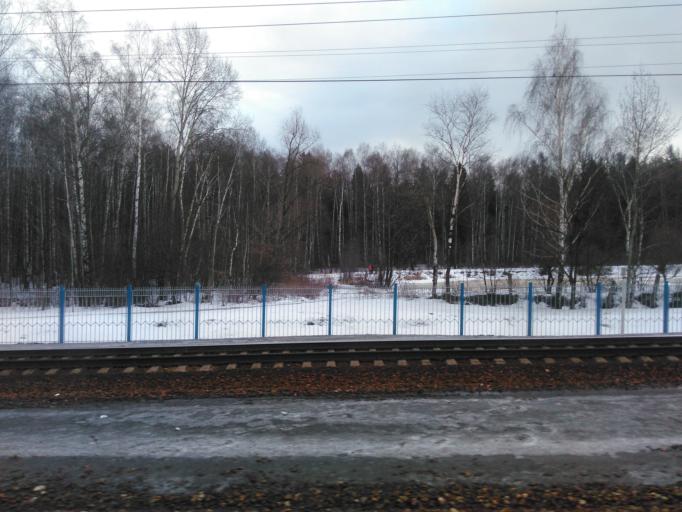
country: RU
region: Moskovskaya
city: Cherkizovo
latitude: 55.9462
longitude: 37.7983
